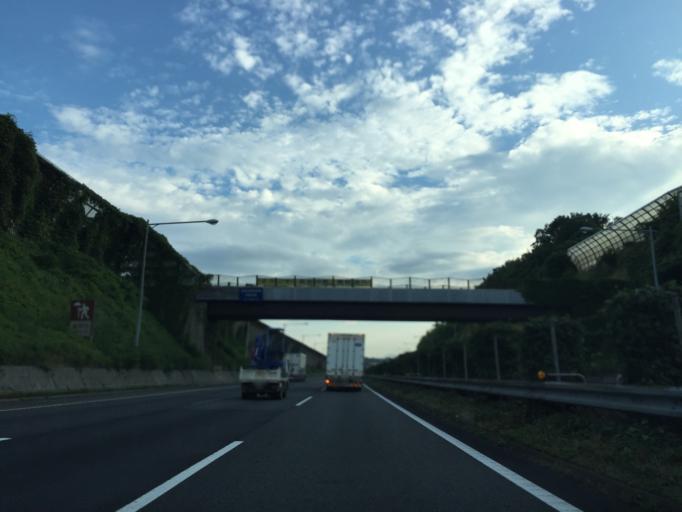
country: JP
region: Kanagawa
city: Isehara
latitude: 35.3866
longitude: 139.2768
